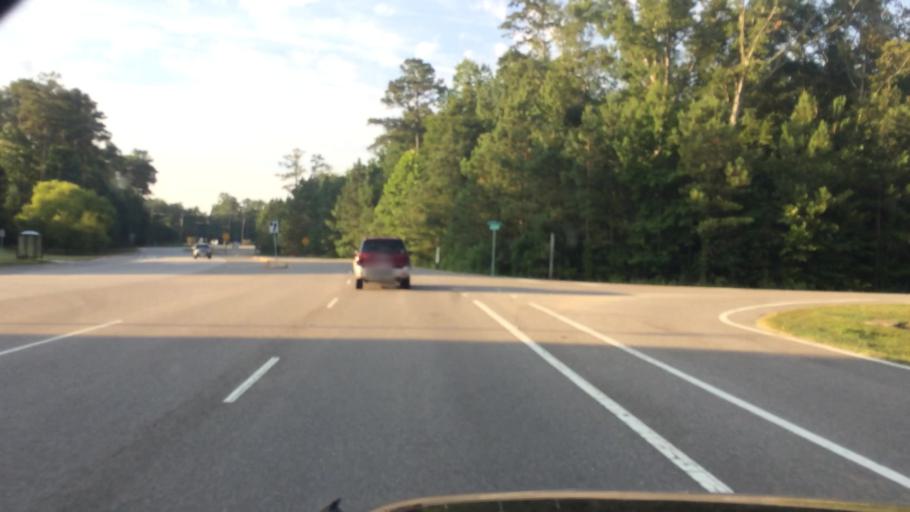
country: US
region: Virginia
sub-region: James City County
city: Williamsburg
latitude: 37.3339
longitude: -76.7364
